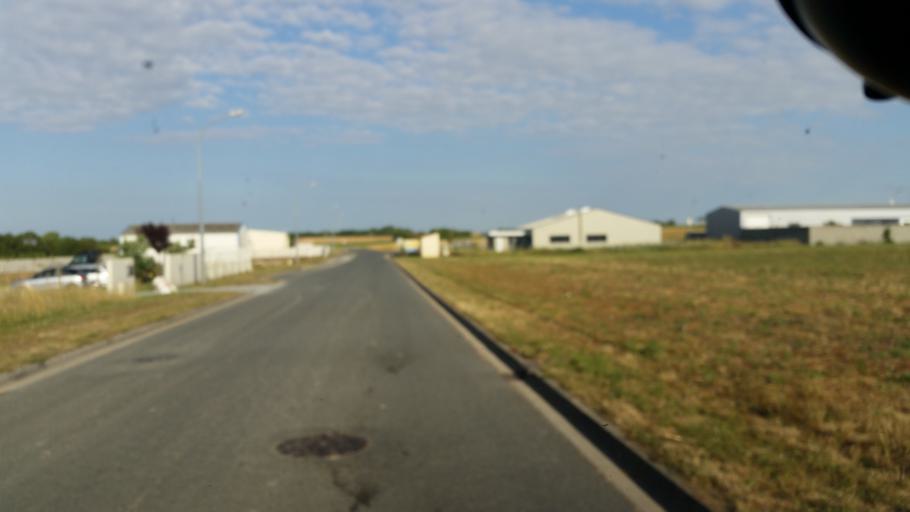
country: FR
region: Poitou-Charentes
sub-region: Departement de la Charente-Maritime
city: Saint-Jean-de-Liversay
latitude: 46.2302
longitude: -0.8832
